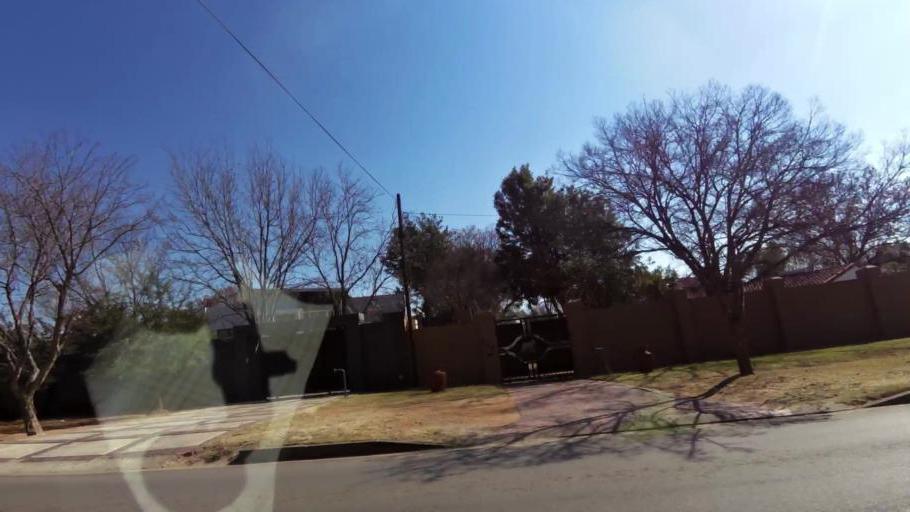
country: ZA
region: Gauteng
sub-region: City of Johannesburg Metropolitan Municipality
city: Roodepoort
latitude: -26.1394
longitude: 27.9389
